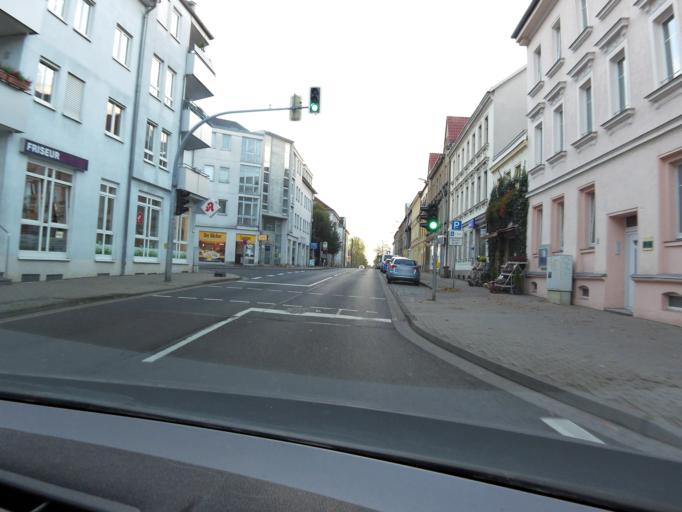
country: DE
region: Saxony
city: Leipzig
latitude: 51.3922
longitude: 12.3284
